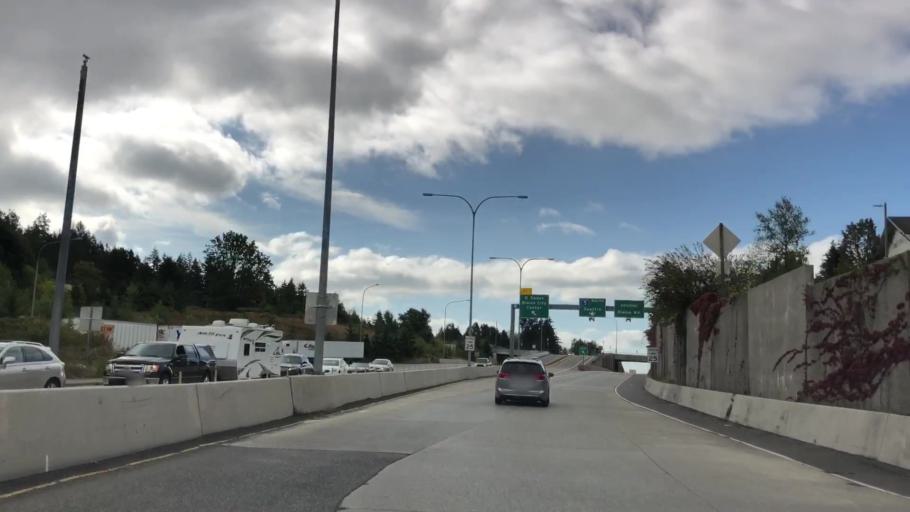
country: US
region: Washington
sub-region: Whatcom County
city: Blaine
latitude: 49.0007
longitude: -122.7354
